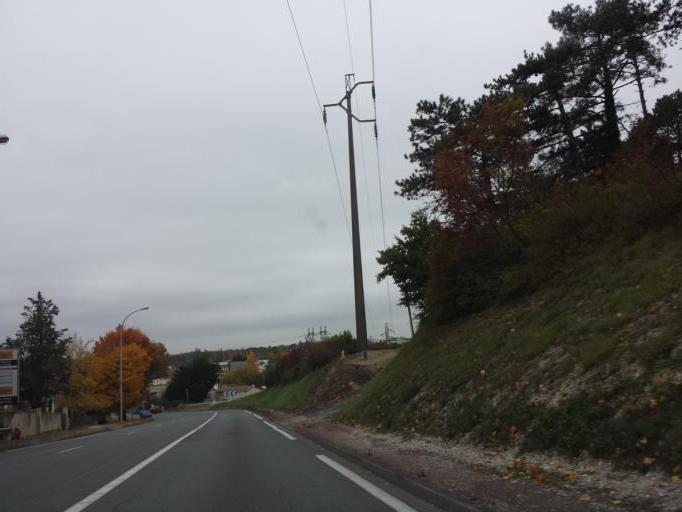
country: FR
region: Poitou-Charentes
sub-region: Departement de la Charente
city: Angouleme
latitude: 45.6334
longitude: 0.1313
